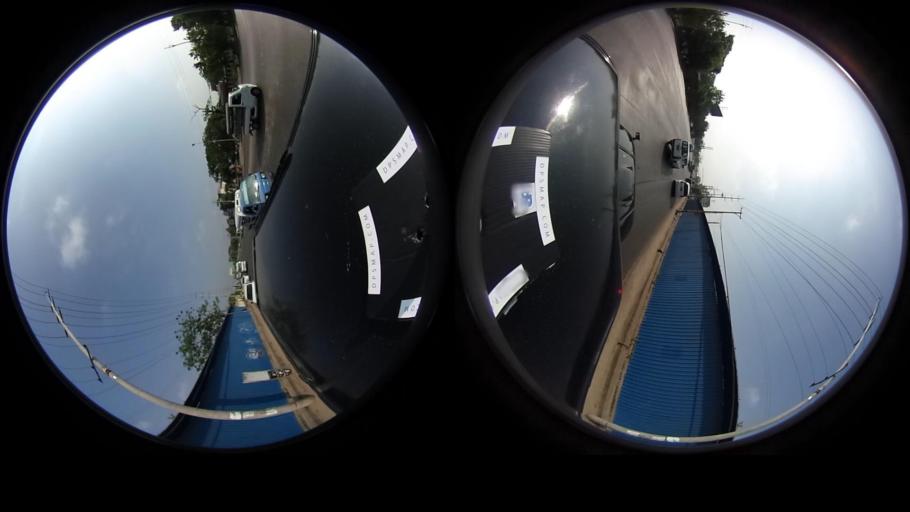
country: MM
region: Yangon
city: Yangon
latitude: 16.8156
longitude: 96.1898
